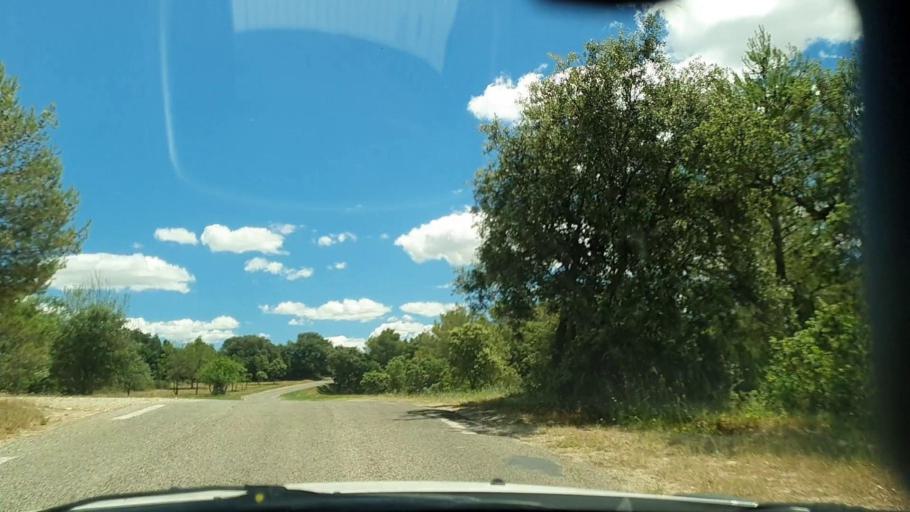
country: FR
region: Languedoc-Roussillon
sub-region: Departement du Gard
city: Cabrieres
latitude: 43.9104
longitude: 4.4469
